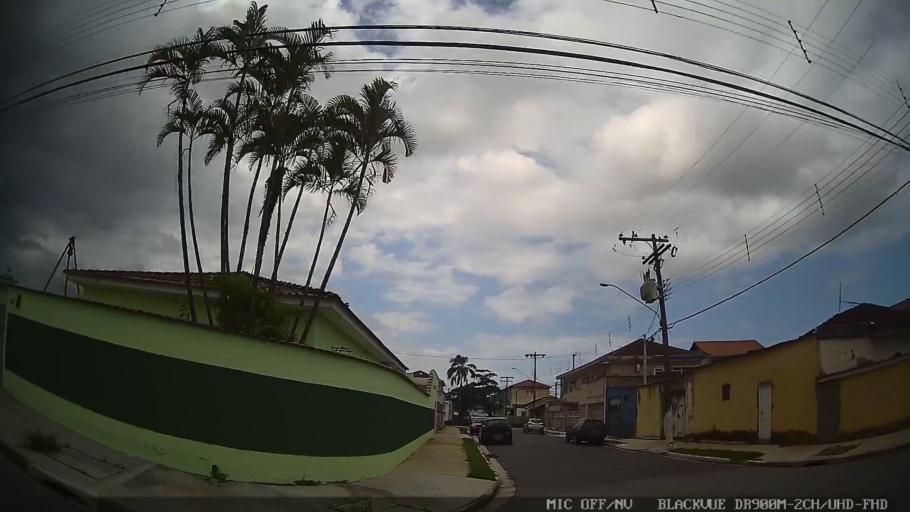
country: BR
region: Sao Paulo
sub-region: Guaruja
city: Guaruja
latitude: -23.9929
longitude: -46.2902
